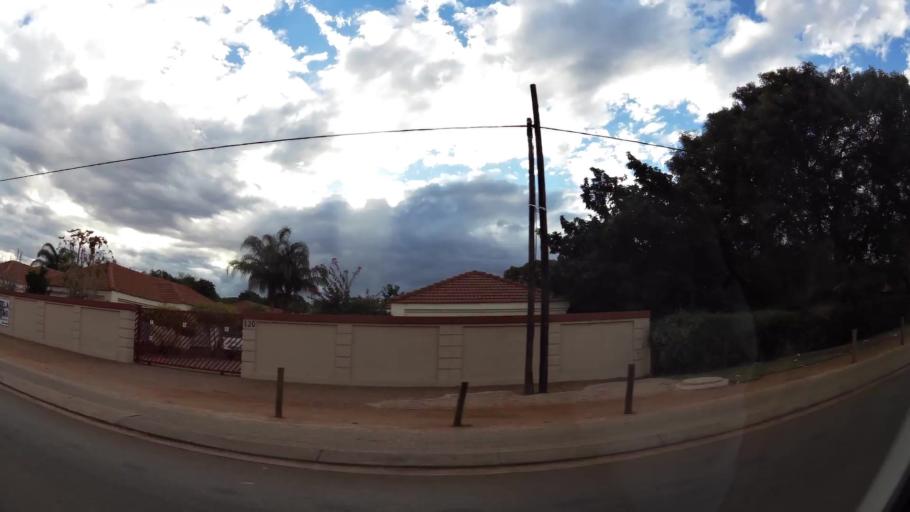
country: ZA
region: Limpopo
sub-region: Waterberg District Municipality
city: Modimolle
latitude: -24.5131
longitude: 28.7208
